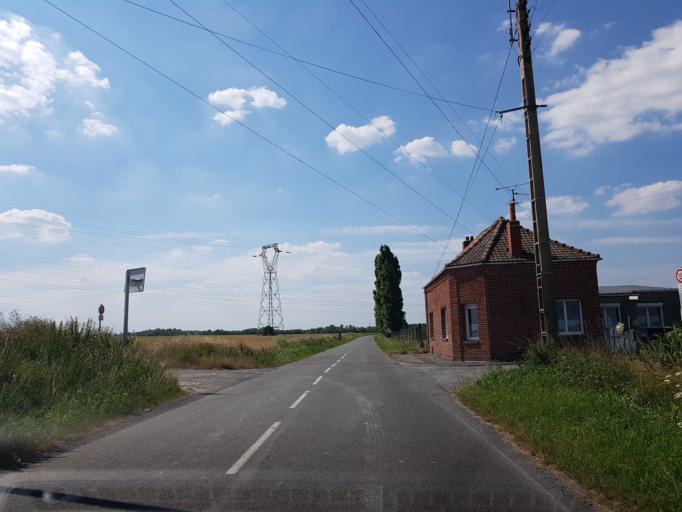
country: FR
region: Nord-Pas-de-Calais
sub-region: Departement du Nord
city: Roeulx
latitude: 50.3181
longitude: 3.3244
